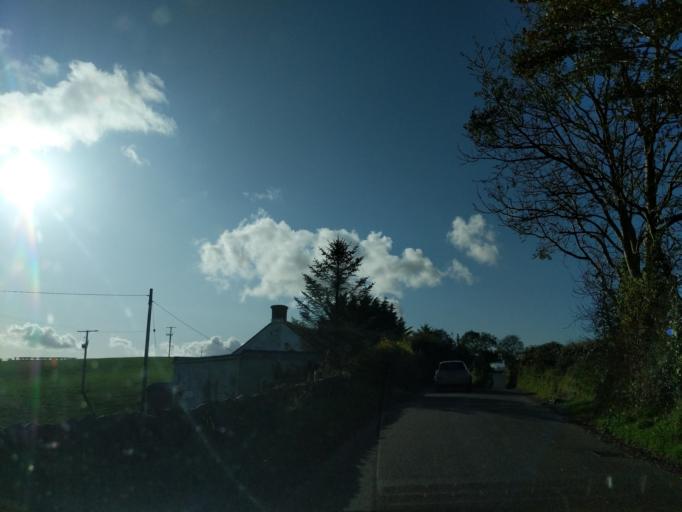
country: GB
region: Scotland
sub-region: Dumfries and Galloway
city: Dalbeattie
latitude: 54.9977
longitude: -3.8262
